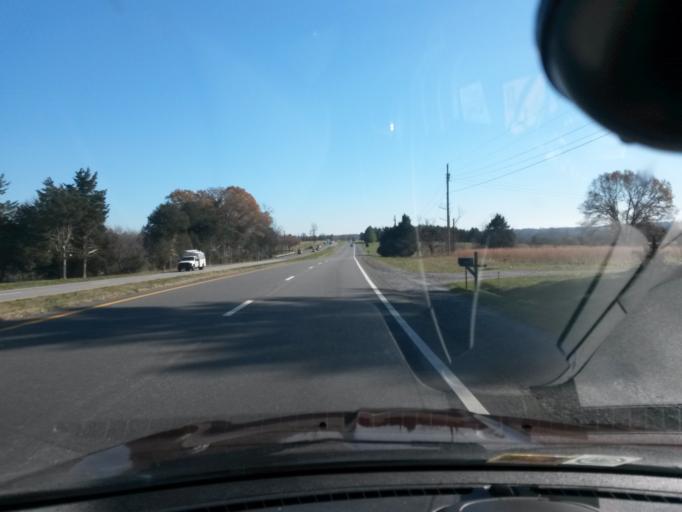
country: US
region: Virginia
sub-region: City of Bedford
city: Bedford
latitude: 37.3185
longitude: -79.4198
